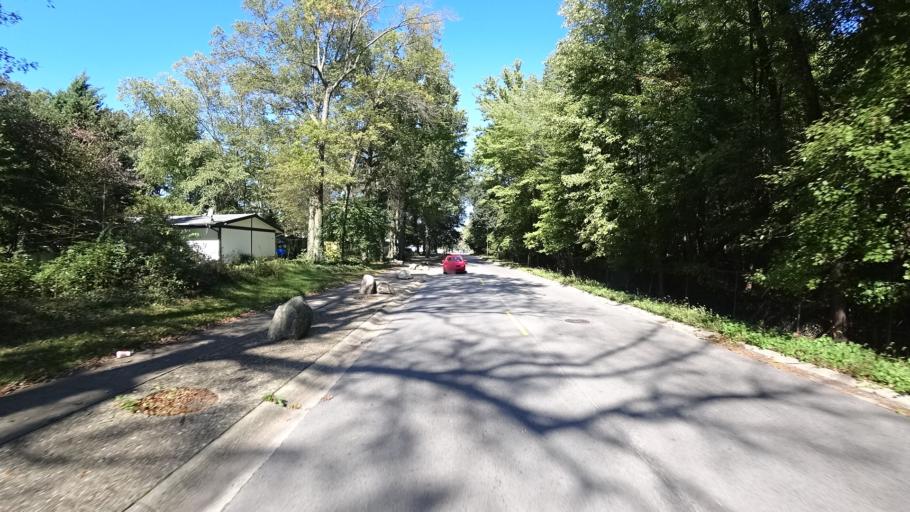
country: US
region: Indiana
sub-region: LaPorte County
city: Michigan City
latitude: 41.6897
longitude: -86.8843
